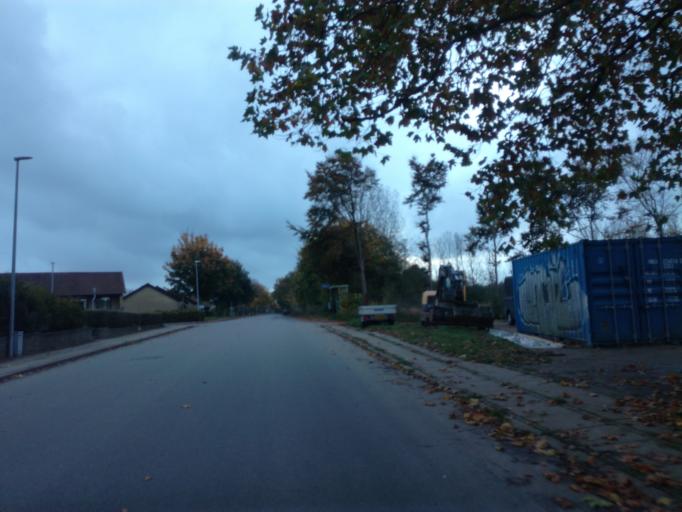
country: DK
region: South Denmark
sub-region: Vejle Kommune
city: Borkop
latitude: 55.6436
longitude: 9.6551
